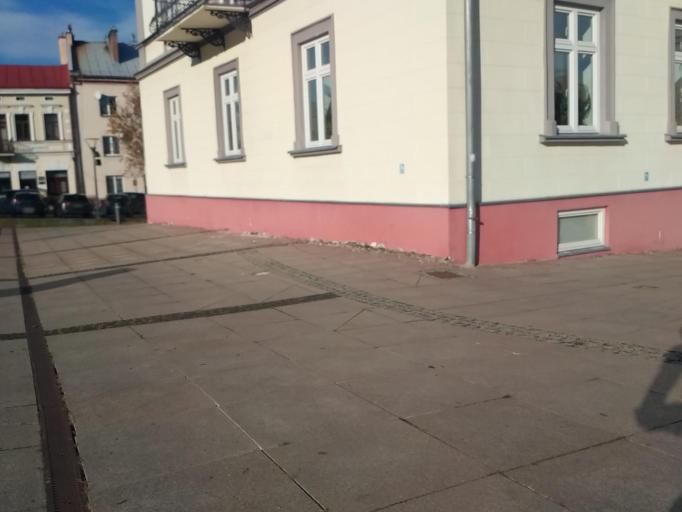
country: PL
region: Subcarpathian Voivodeship
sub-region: Powiat brzozowski
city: Brzozow
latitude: 49.6969
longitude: 22.0213
